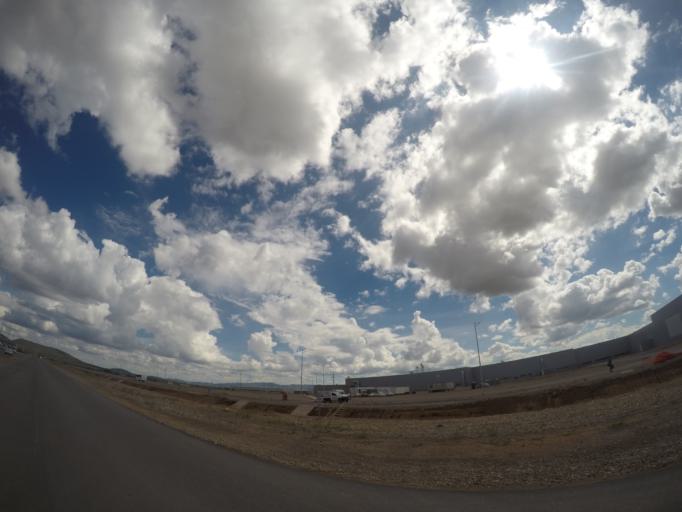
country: MX
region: San Luis Potosi
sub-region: Zaragoza
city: Cerro Gordo
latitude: 21.9670
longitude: -100.8478
